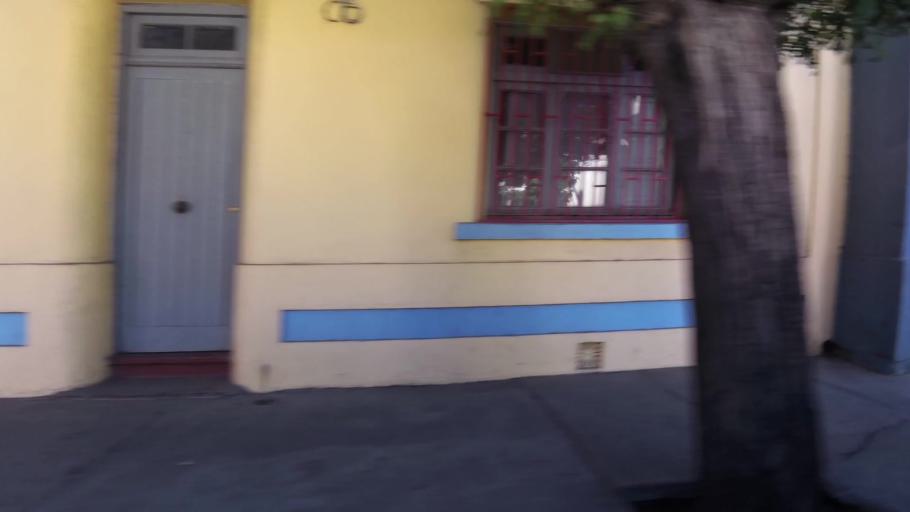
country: CL
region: O'Higgins
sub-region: Provincia de Cachapoal
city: Rancagua
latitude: -34.1735
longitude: -70.7372
